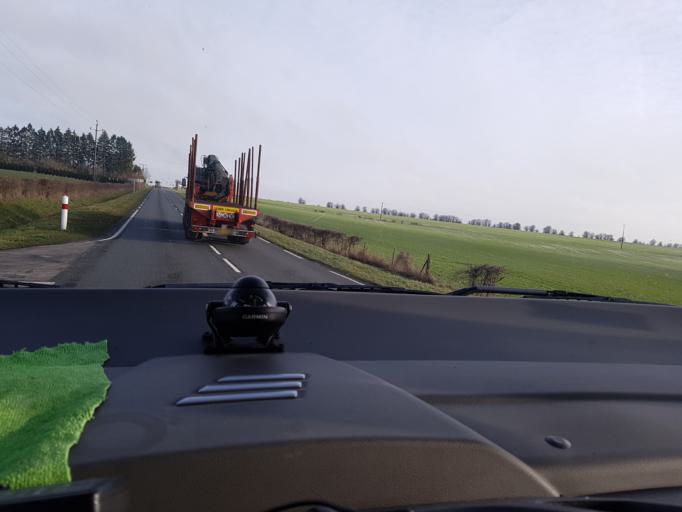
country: FR
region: Champagne-Ardenne
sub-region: Departement des Ardennes
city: Signy-le-Petit
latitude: 49.8630
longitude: 4.2450
